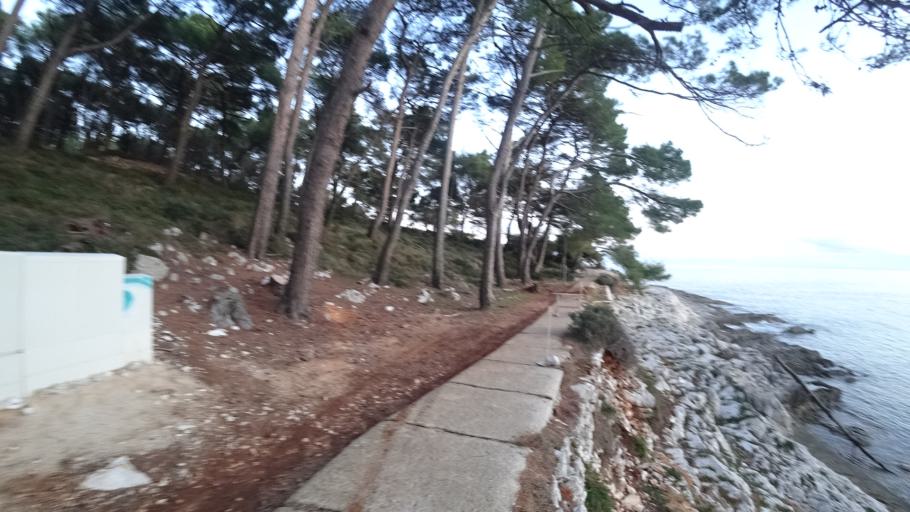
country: HR
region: Primorsko-Goranska
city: Mali Losinj
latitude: 44.5242
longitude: 14.4542
